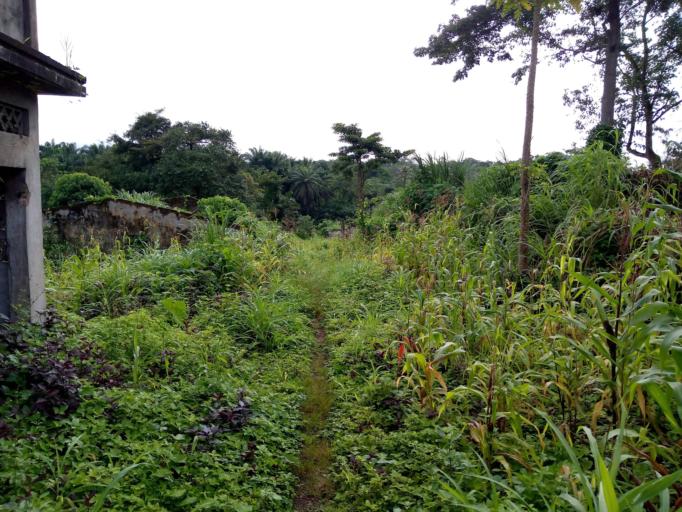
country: SL
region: Eastern Province
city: Buedu
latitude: 8.4659
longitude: -10.3380
